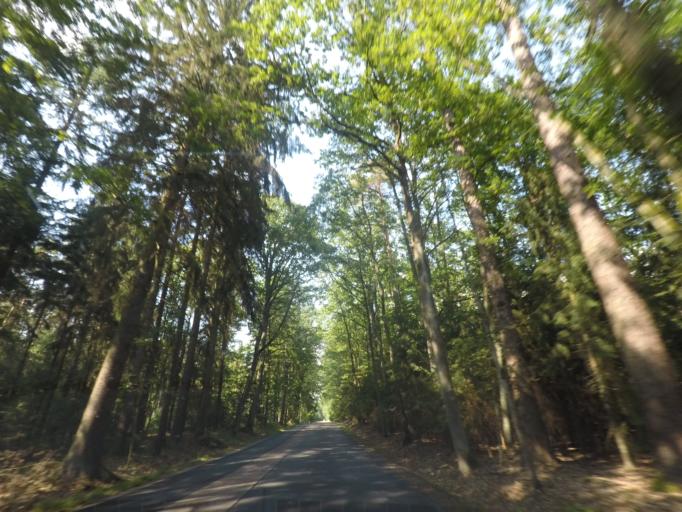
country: CZ
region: Pardubicky
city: Horni Jeleni
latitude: 50.0220
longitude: 16.0815
